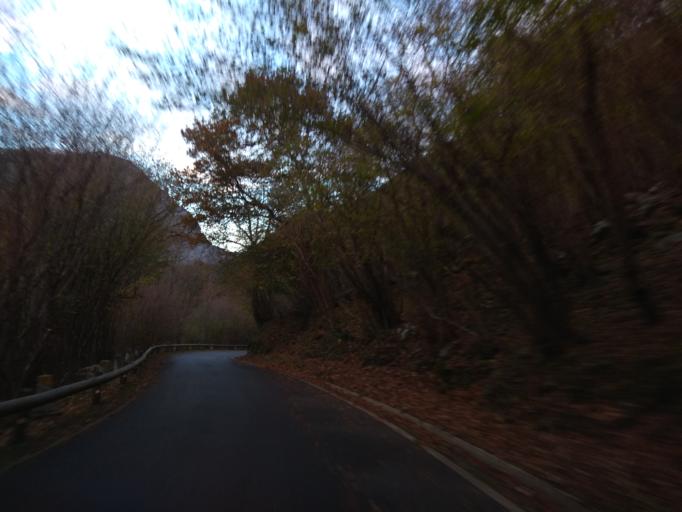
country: ES
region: Cantabria
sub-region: Provincia de Cantabria
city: Arredondo
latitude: 43.2292
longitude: -3.6017
